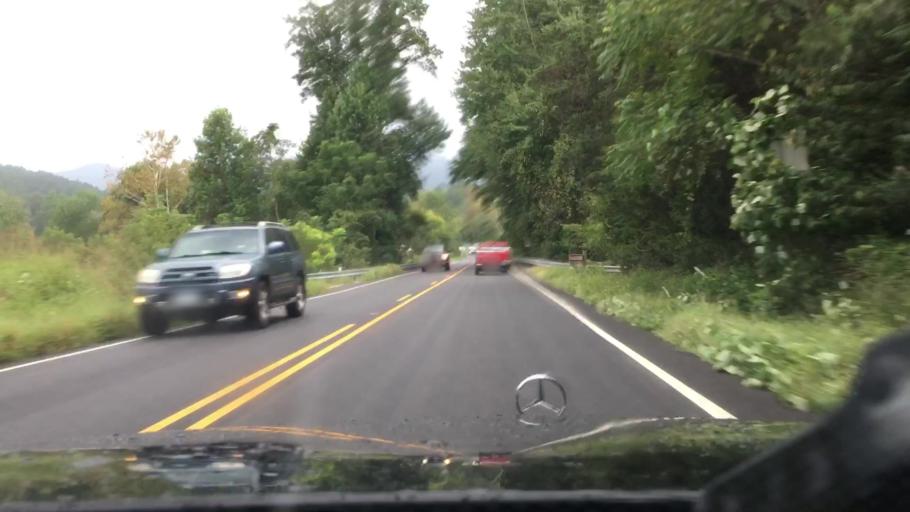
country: US
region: Virginia
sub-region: Nelson County
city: Nellysford
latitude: 37.9045
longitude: -78.8547
